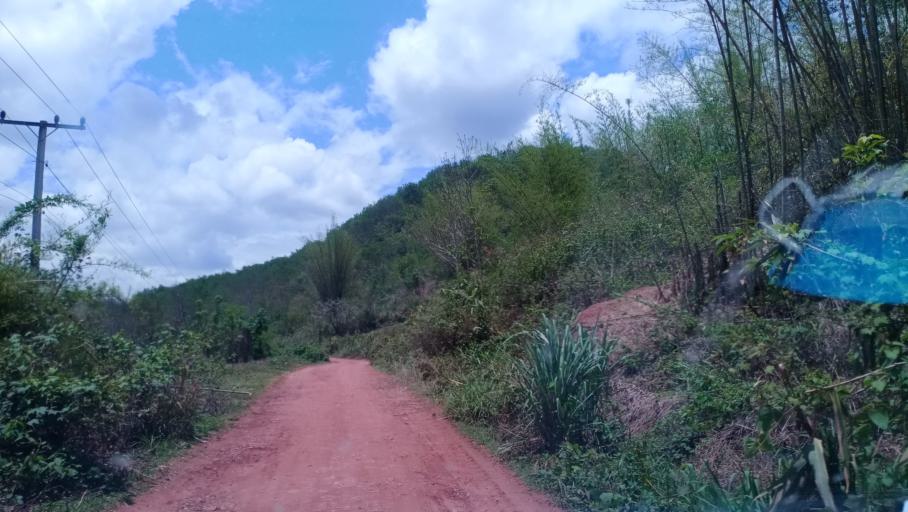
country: CN
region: Yunnan
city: Menglie
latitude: 22.1355
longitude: 101.7852
